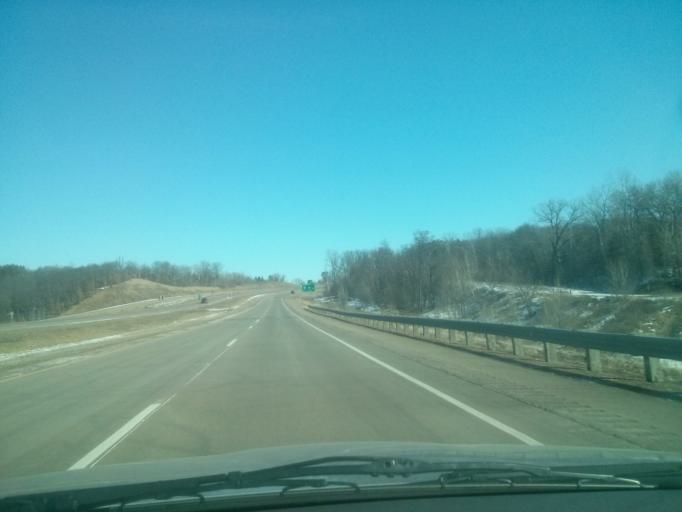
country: US
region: Wisconsin
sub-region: Saint Croix County
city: Somerset
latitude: 45.1010
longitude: -92.7317
